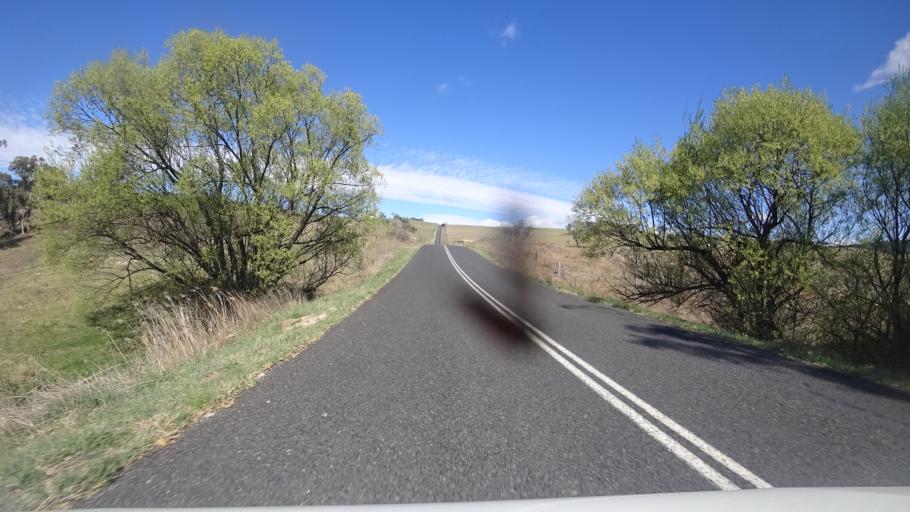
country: AU
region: New South Wales
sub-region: Lithgow
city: Bowenfels
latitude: -33.5198
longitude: 149.9823
